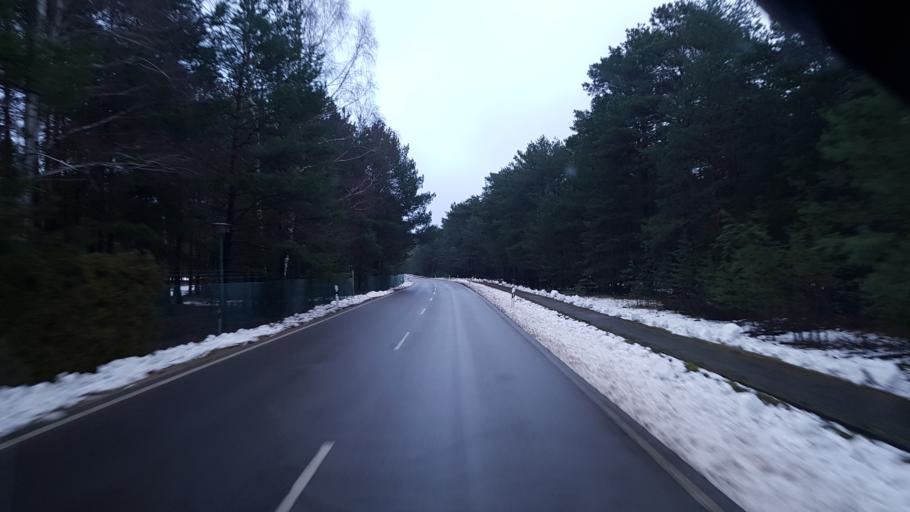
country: DE
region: Brandenburg
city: Janschwalde
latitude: 51.8802
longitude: 14.5232
